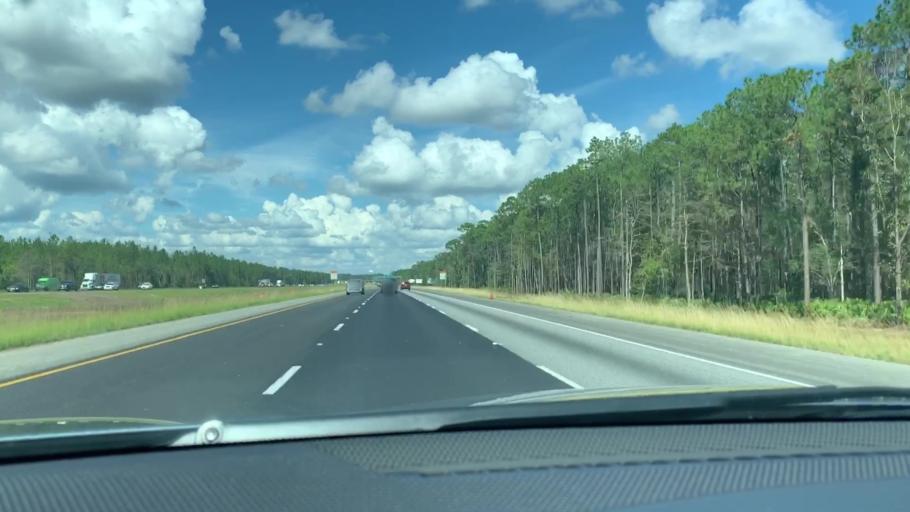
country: US
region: Georgia
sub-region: Camden County
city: Woodbine
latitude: 30.9275
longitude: -81.6858
